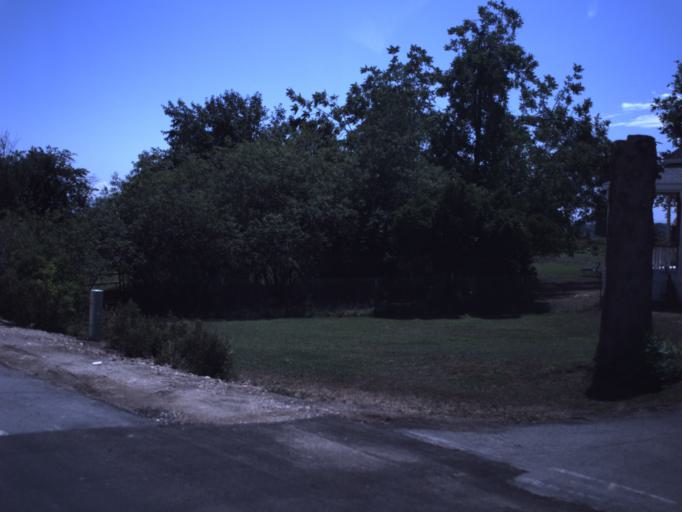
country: US
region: Utah
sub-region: Uintah County
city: Maeser
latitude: 40.4626
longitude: -109.5763
